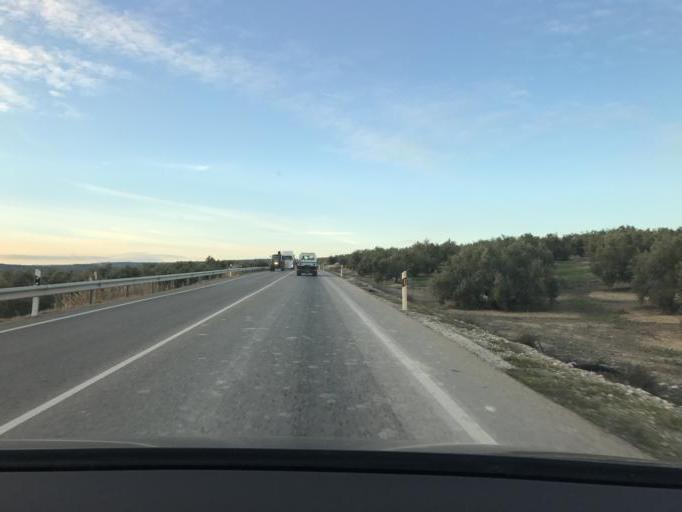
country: ES
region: Andalusia
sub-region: Provincia de Jaen
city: Ubeda
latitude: 37.9754
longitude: -3.3772
